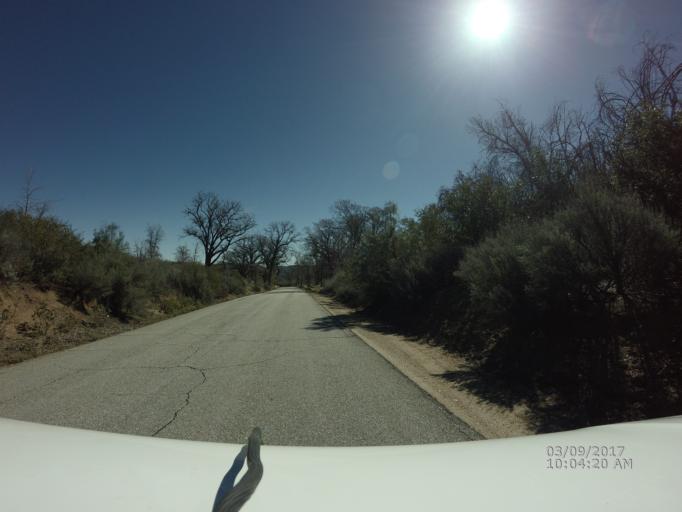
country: US
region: California
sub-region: Los Angeles County
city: Castaic
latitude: 34.7346
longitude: -118.6388
